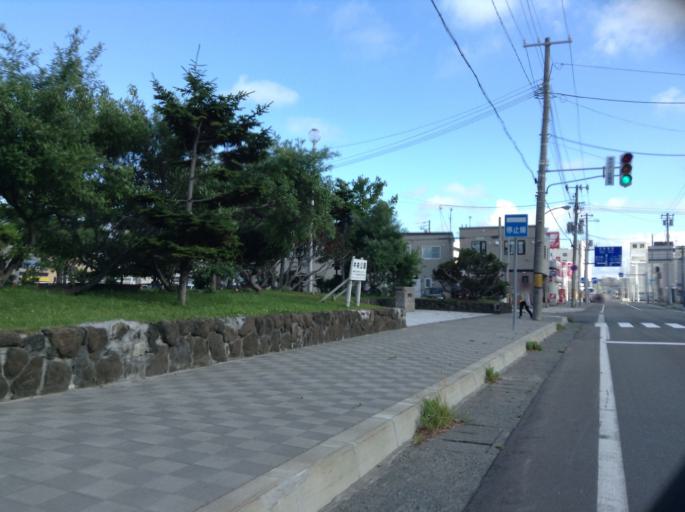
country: JP
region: Hokkaido
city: Wakkanai
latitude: 45.4190
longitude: 141.6763
